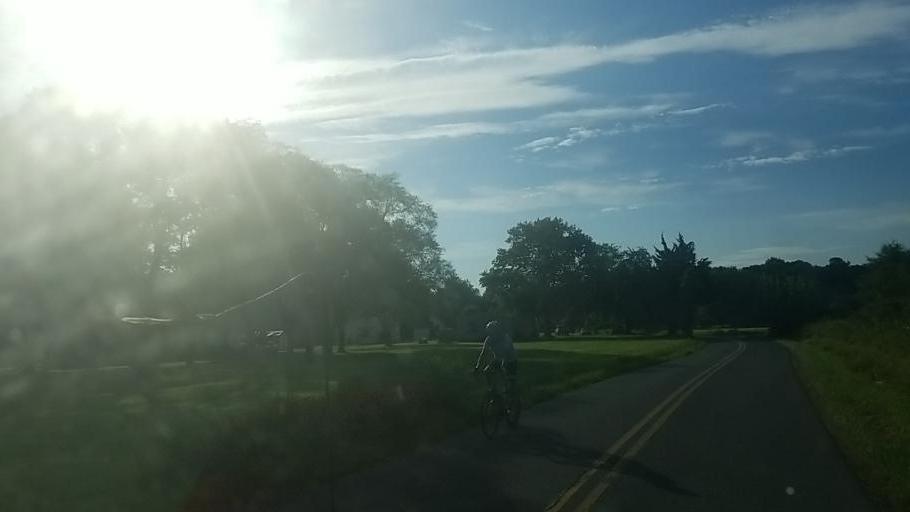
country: US
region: Maryland
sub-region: Worcester County
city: Berlin
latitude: 38.3138
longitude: -75.1624
